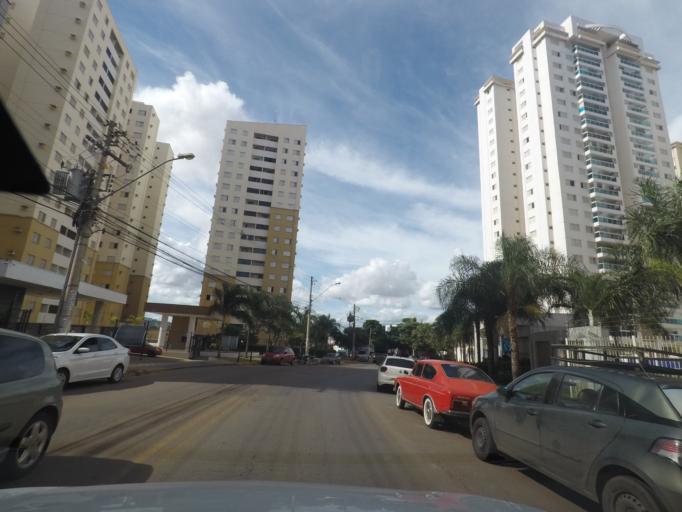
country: BR
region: Goias
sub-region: Goiania
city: Goiania
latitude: -16.7058
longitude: -49.3285
